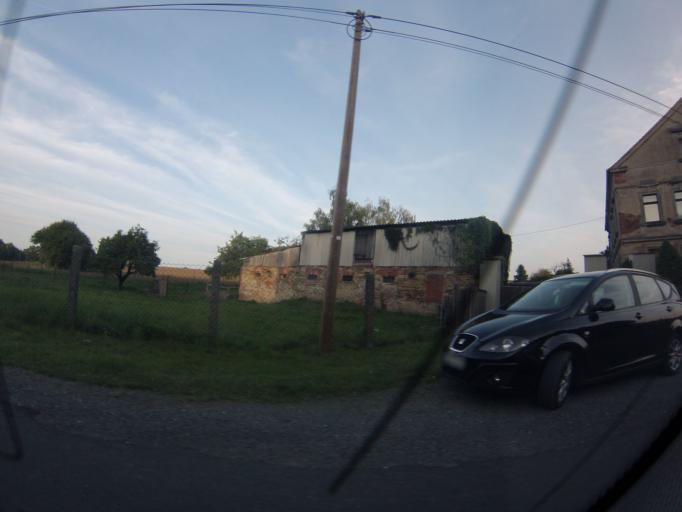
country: DE
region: Thuringia
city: Altkirchen
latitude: 50.9254
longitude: 12.3407
